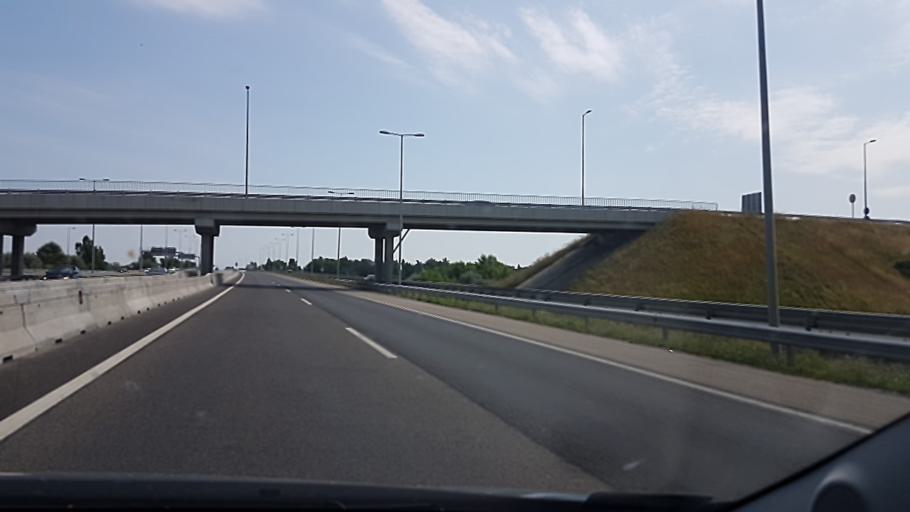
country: HU
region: Budapest
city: Budapest XVIII. keruelet
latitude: 47.4150
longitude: 19.1553
